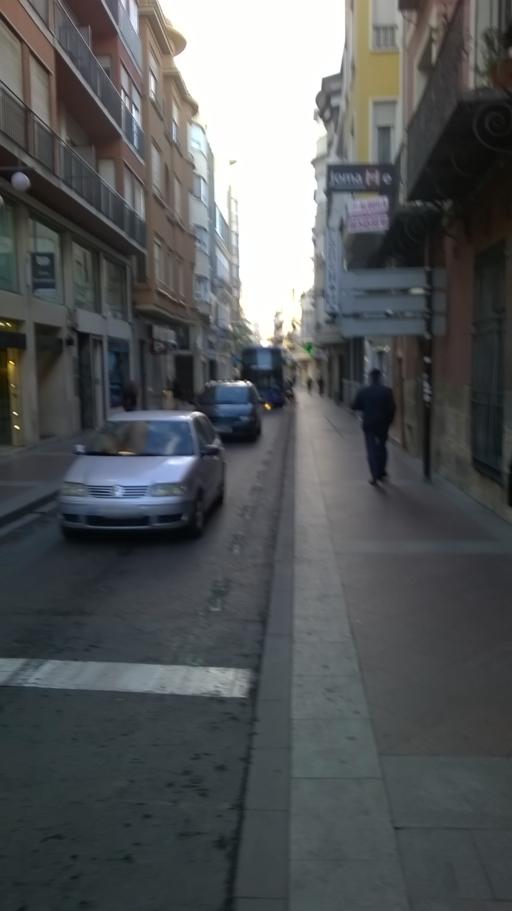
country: ES
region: Valencia
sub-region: Provincia de Alicante
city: Elche
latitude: 38.2666
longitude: -0.6951
